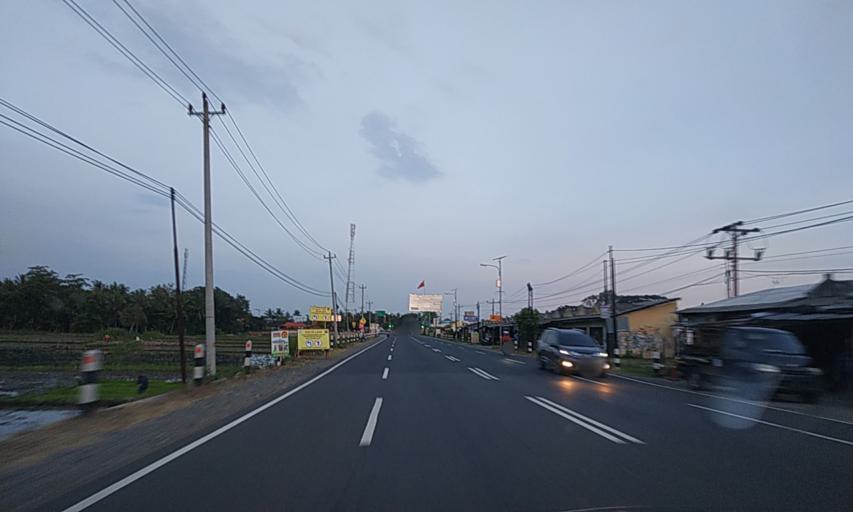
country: ID
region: Daerah Istimewa Yogyakarta
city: Srandakan
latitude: -7.8749
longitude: 110.2031
